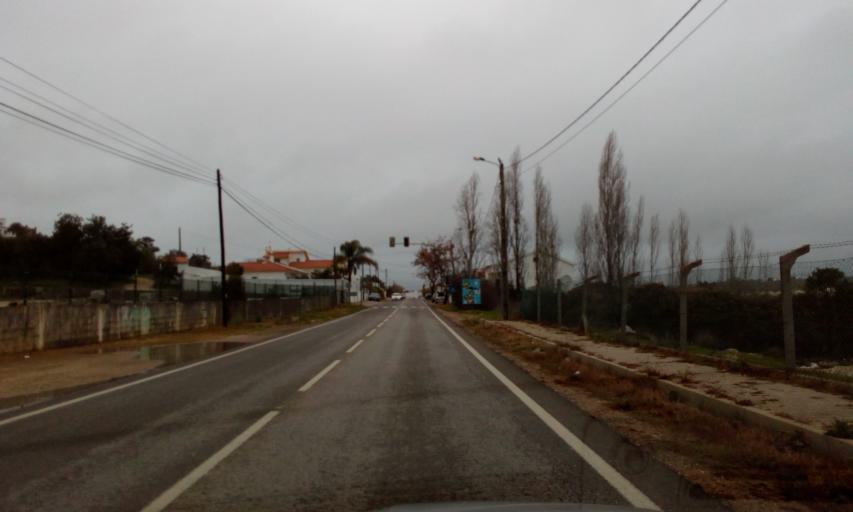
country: PT
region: Faro
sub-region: Albufeira
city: Guia
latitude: 37.1600
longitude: -8.2960
